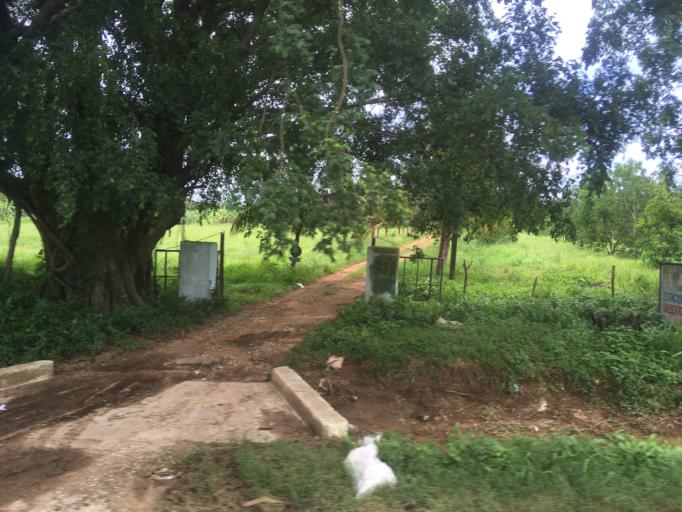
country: CU
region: Matanzas
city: Colon
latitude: 22.7100
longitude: -80.8903
